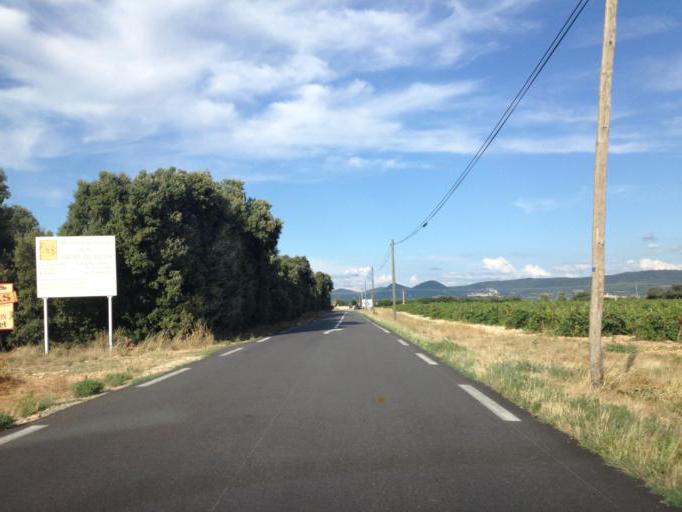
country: FR
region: Provence-Alpes-Cote d'Azur
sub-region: Departement du Vaucluse
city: Violes
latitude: 44.1821
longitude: 4.9494
